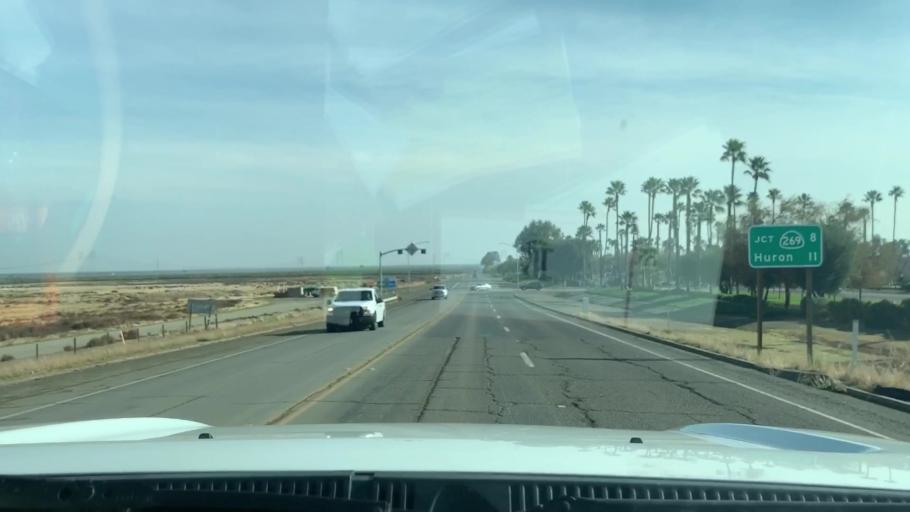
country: US
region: California
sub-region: Fresno County
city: Huron
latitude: 36.2544
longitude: -120.2401
